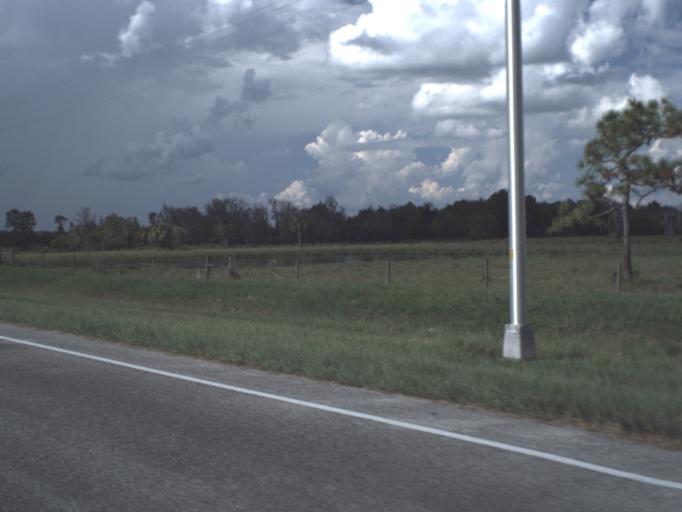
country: US
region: Florida
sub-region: Polk County
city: Babson Park
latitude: 27.8533
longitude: -81.3686
